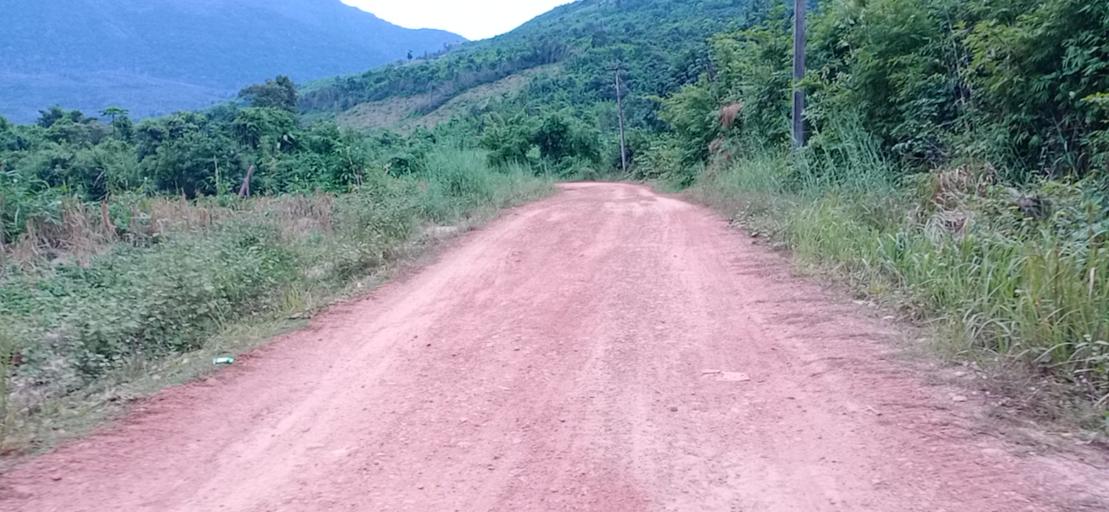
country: TH
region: Changwat Bueng Kan
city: Pak Khat
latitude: 18.5541
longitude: 103.1760
